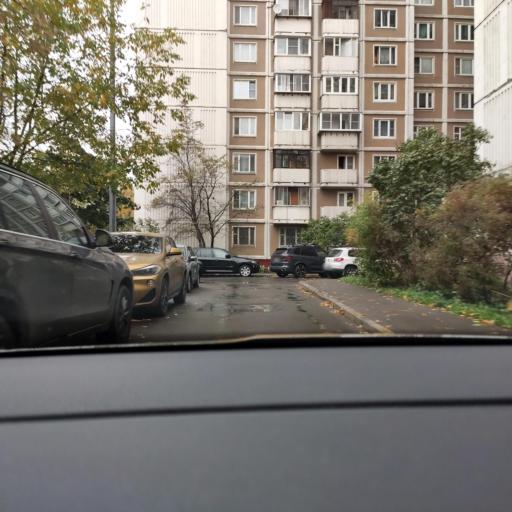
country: RU
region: Moscow
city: Zhulebino
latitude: 55.7005
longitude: 37.8443
